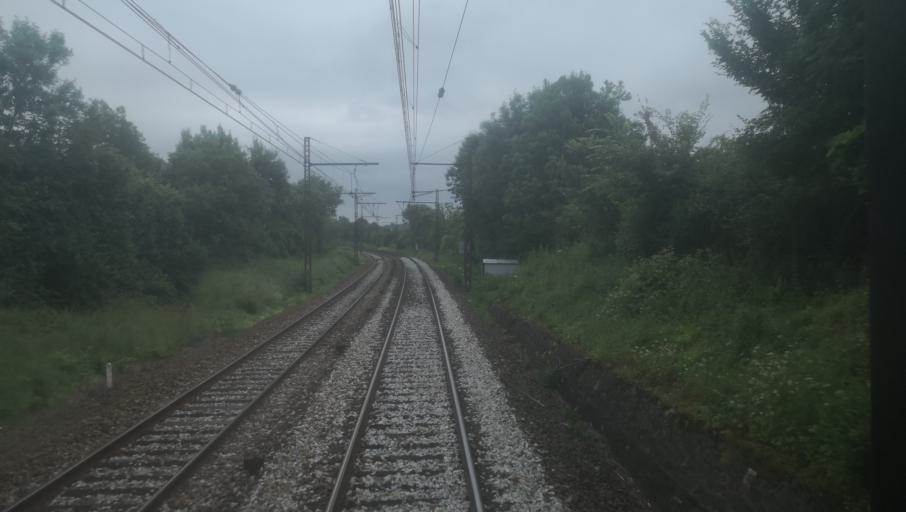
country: FR
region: Centre
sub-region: Departement de l'Indre
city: Le Pechereau
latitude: 46.5275
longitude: 1.5257
